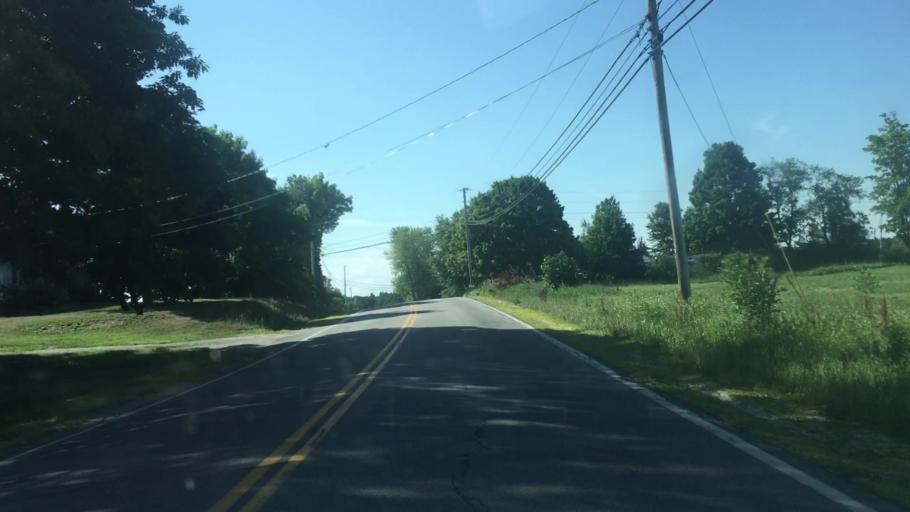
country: US
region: Maine
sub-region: York County
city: Buxton
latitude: 43.6261
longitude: -70.5502
